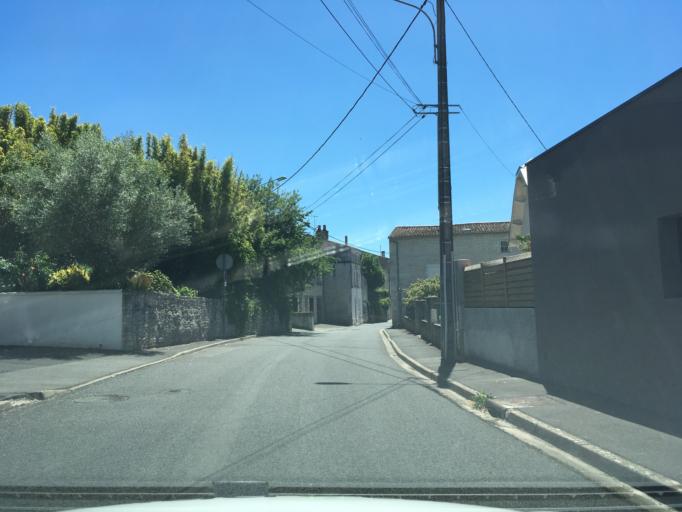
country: FR
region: Poitou-Charentes
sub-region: Departement des Deux-Sevres
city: Aiffres
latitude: 46.3279
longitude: -0.4227
